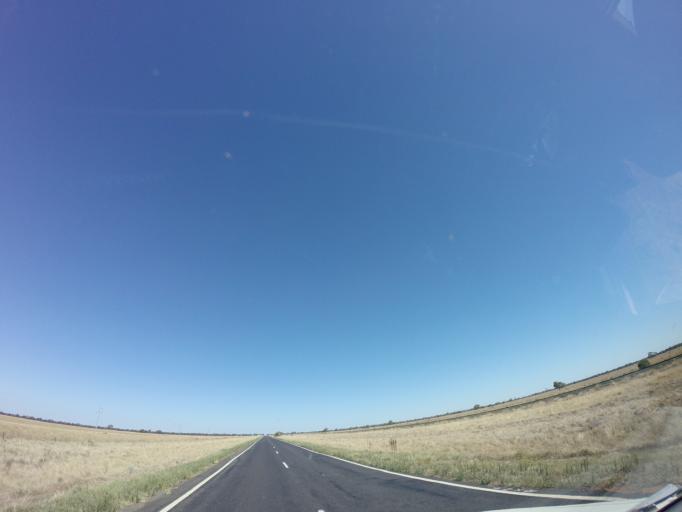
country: AU
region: New South Wales
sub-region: Bogan
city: Nyngan
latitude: -31.6726
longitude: 147.4047
